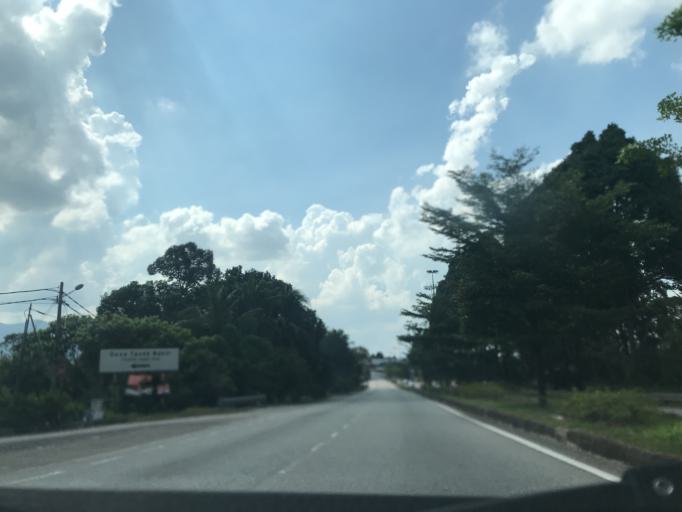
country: MY
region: Perak
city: Ipoh
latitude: 4.6354
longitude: 101.1142
